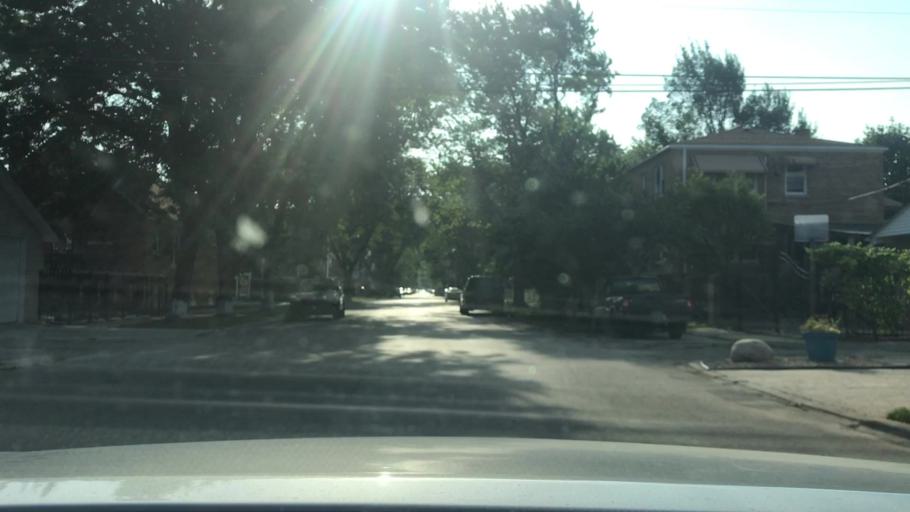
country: US
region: Illinois
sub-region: Cook County
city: Evergreen Park
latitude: 41.7608
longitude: -87.6975
